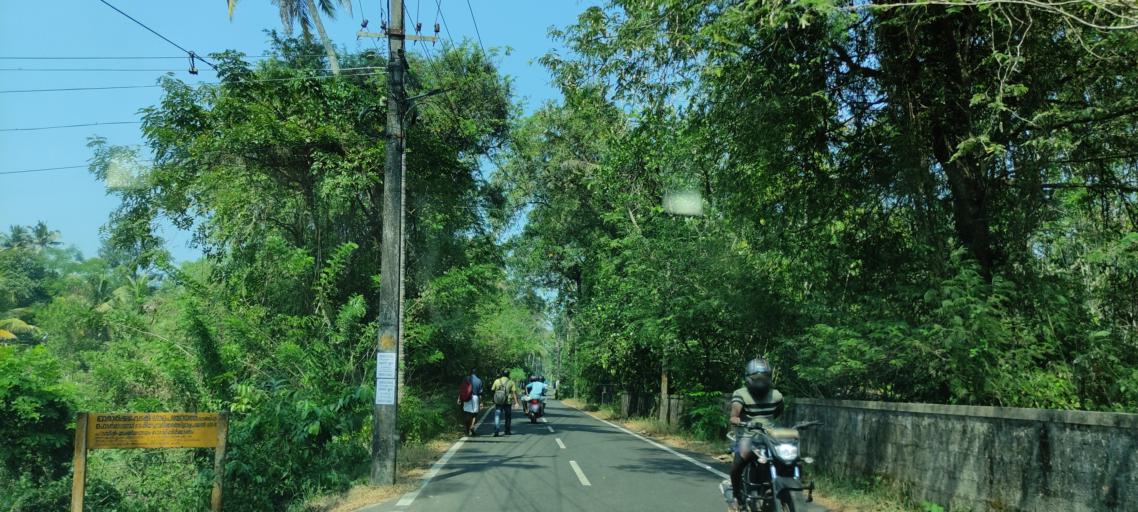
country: IN
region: Kerala
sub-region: Alappuzha
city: Shertallai
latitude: 9.5984
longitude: 76.3117
